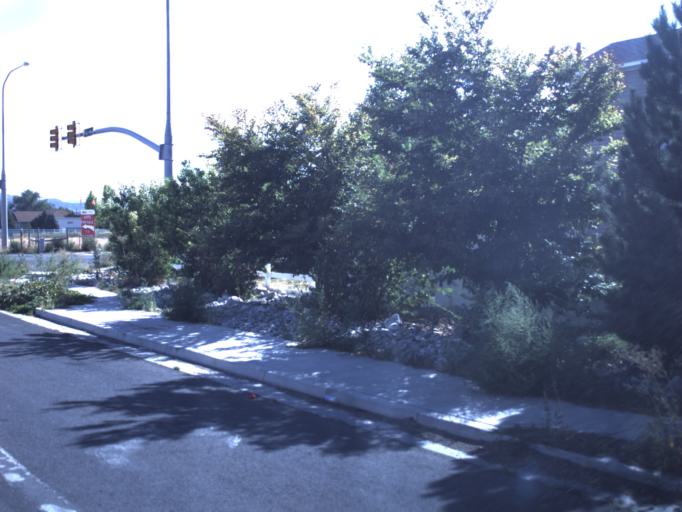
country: US
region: Utah
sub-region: Tooele County
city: Grantsville
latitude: 40.6001
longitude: -112.4260
